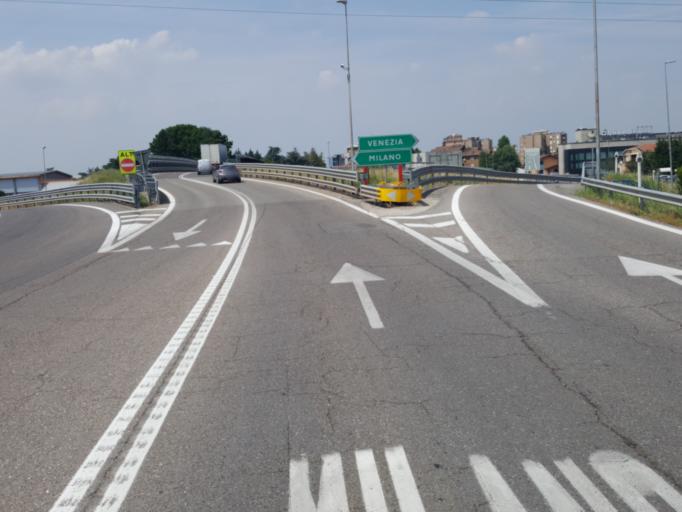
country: IT
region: Lombardy
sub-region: Provincia di Monza e Brianza
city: Cavenago di Brianza
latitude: 45.5777
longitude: 9.4159
